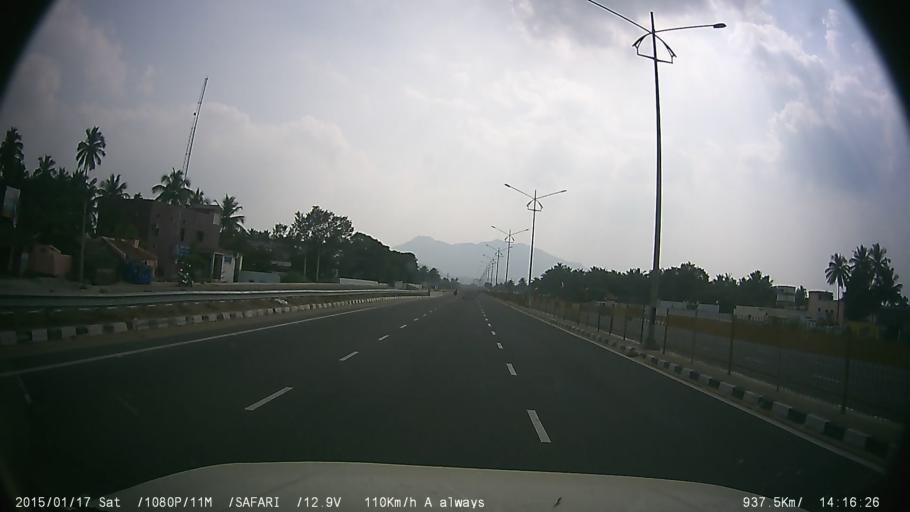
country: IN
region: Tamil Nadu
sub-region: Vellore
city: Ambur
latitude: 12.7545
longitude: 78.6991
